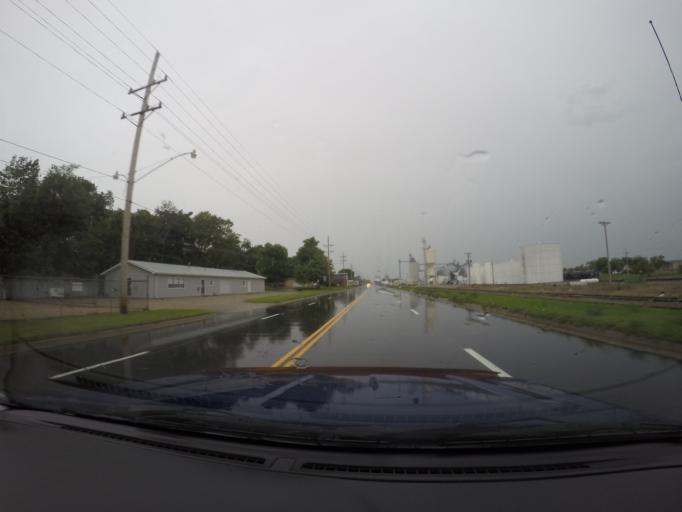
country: US
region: Kansas
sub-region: Cloud County
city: Concordia
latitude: 39.5736
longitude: -97.6693
